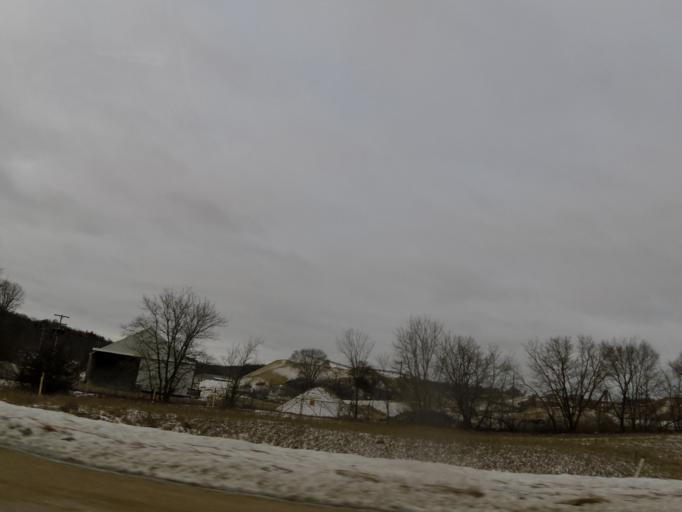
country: US
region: Minnesota
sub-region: Carver County
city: Carver
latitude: 44.7505
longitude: -93.6495
